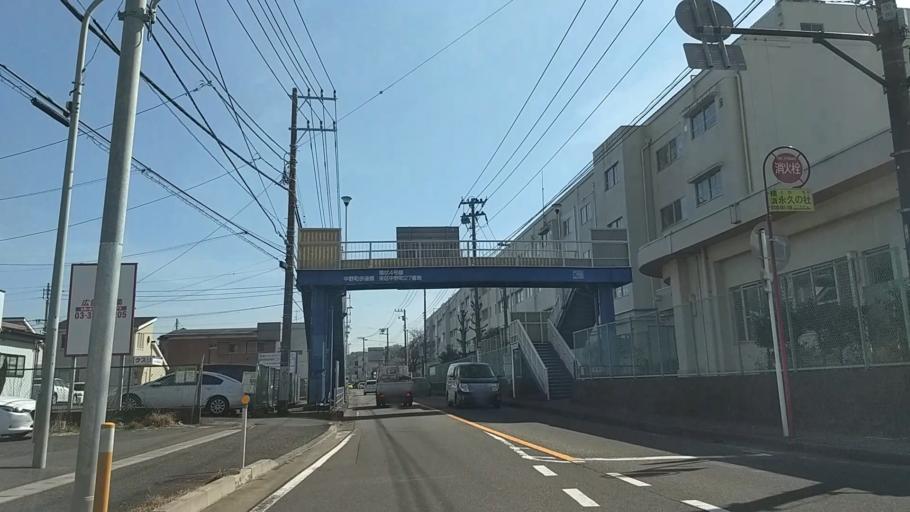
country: JP
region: Kanagawa
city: Kamakura
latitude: 35.3635
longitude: 139.5603
